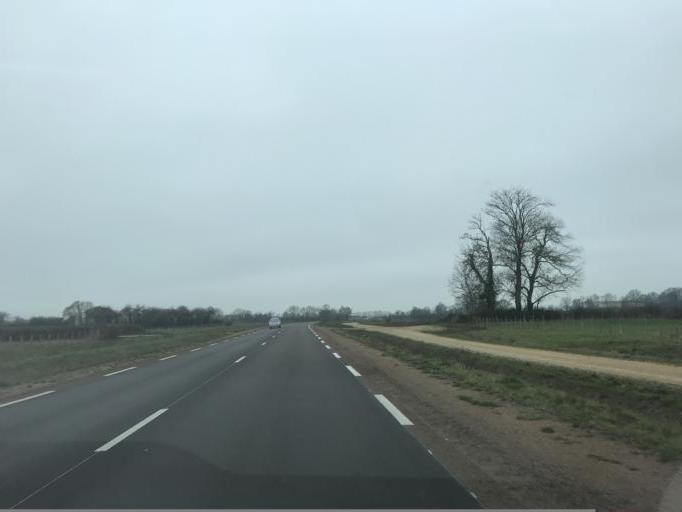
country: FR
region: Bourgogne
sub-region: Departement de l'Yonne
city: Avallon
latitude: 47.5016
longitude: 3.9201
